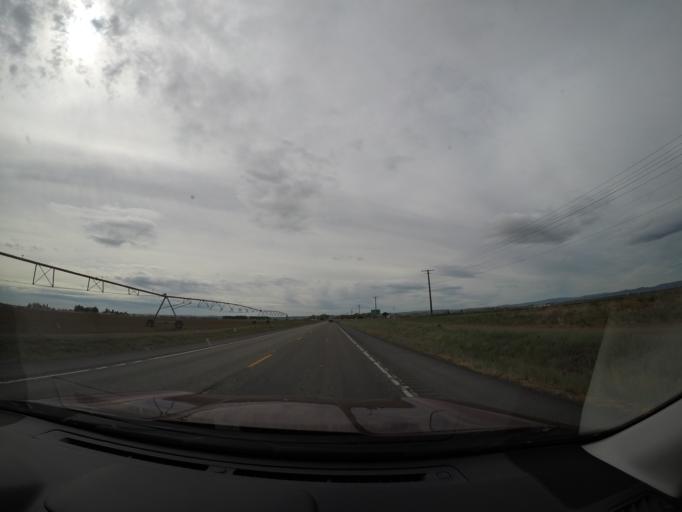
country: US
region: Washington
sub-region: Grant County
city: Quincy
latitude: 47.1131
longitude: -119.8535
